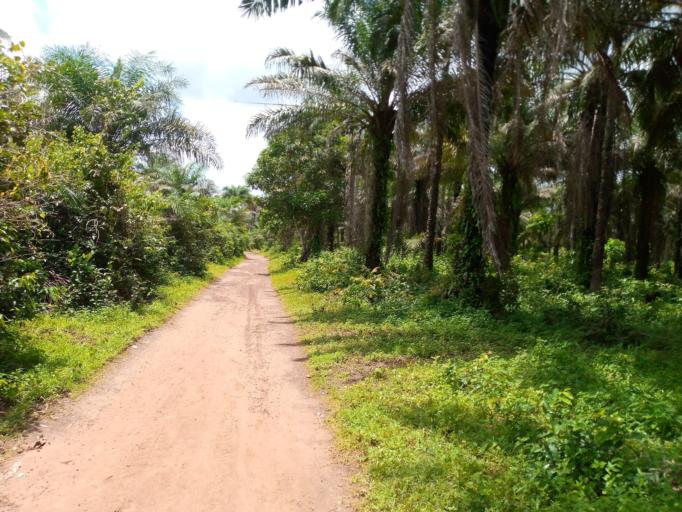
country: SL
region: Northern Province
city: Mange
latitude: 8.9736
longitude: -12.8269
